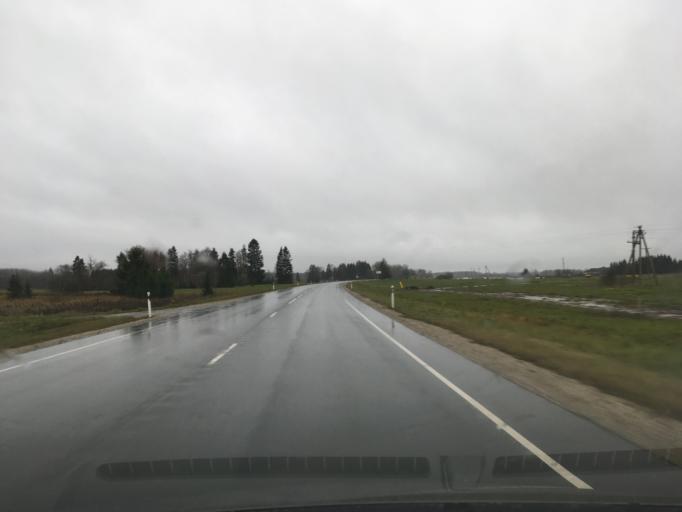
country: EE
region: Harju
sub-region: Nissi vald
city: Turba
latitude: 58.8776
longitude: 24.0872
